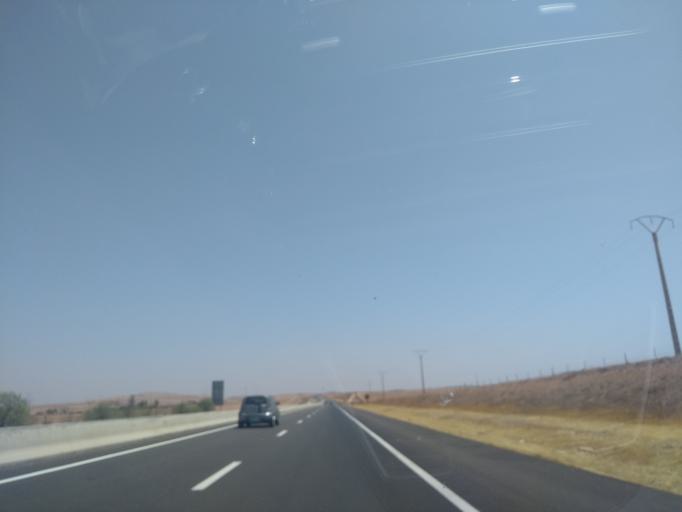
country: MA
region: Marrakech-Tensift-Al Haouz
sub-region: Kelaa-Des-Sraghna
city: Sidi Abdallah
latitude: 32.2880
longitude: -7.9642
